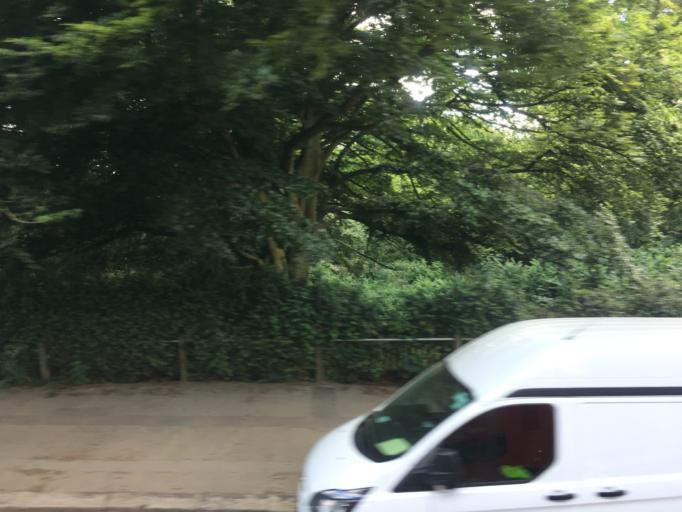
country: GB
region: England
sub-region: Greater London
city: Belsize Park
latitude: 51.5725
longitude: -0.1593
